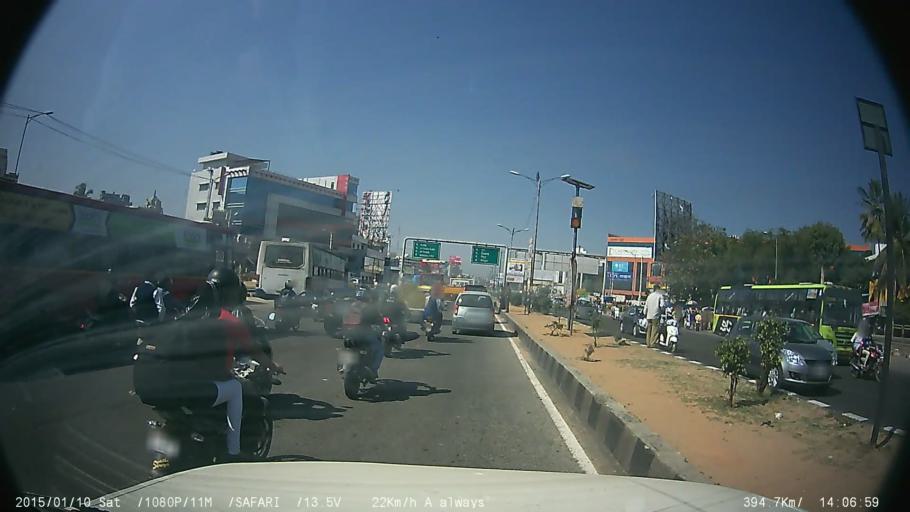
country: IN
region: Karnataka
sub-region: Bangalore Urban
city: Bangalore
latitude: 12.9114
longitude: 77.6262
